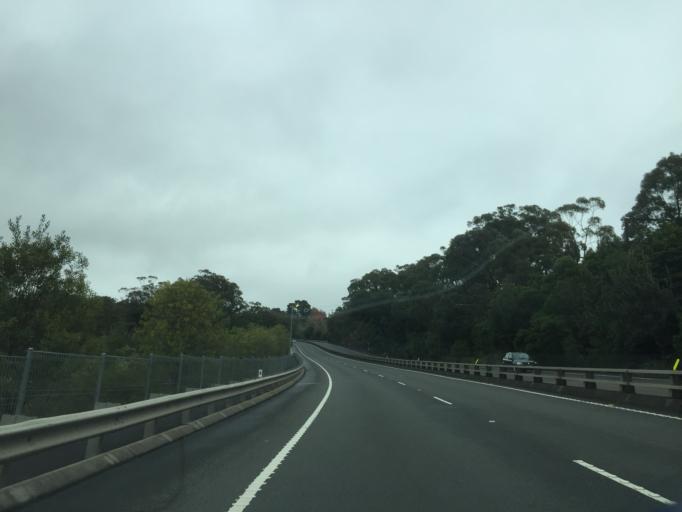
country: AU
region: New South Wales
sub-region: Blue Mountains Municipality
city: Hazelbrook
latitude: -33.7156
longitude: 150.5014
